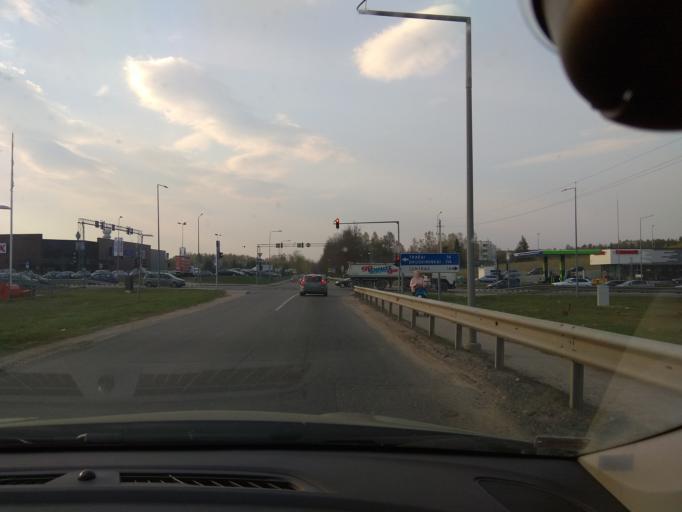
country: LT
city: Grigiskes
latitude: 54.6234
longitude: 25.1118
